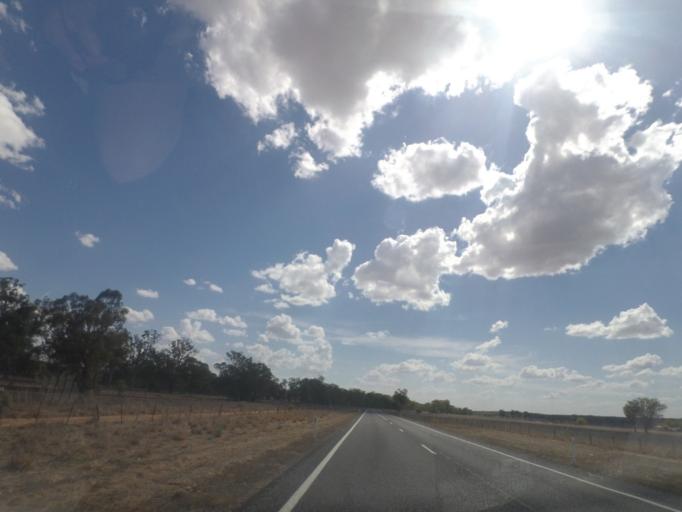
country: AU
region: Queensland
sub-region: Southern Downs
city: Stanthorpe
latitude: -28.3930
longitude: 151.3165
